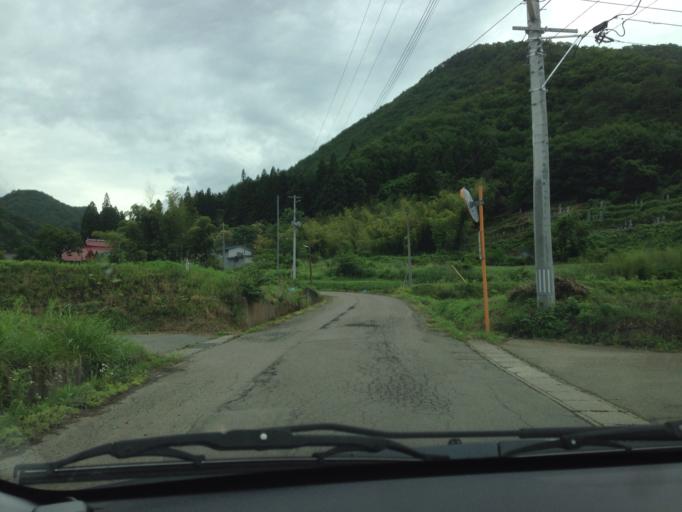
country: JP
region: Fukushima
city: Kitakata
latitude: 37.4030
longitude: 139.9104
